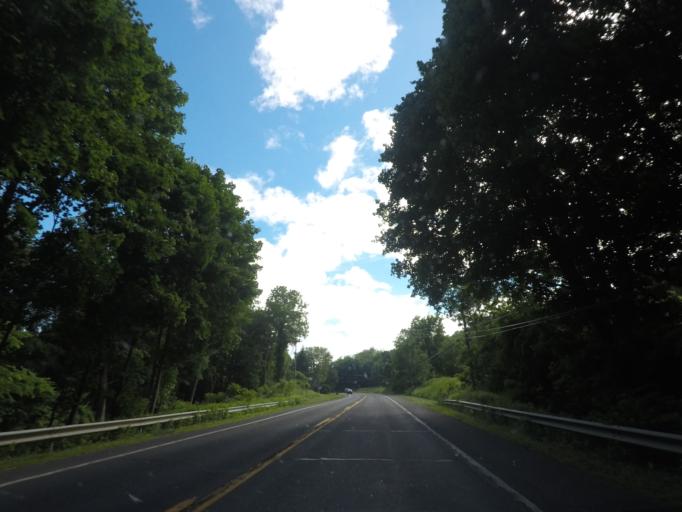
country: US
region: Massachusetts
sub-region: Berkshire County
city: Sheffield
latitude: 42.1159
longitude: -73.5325
